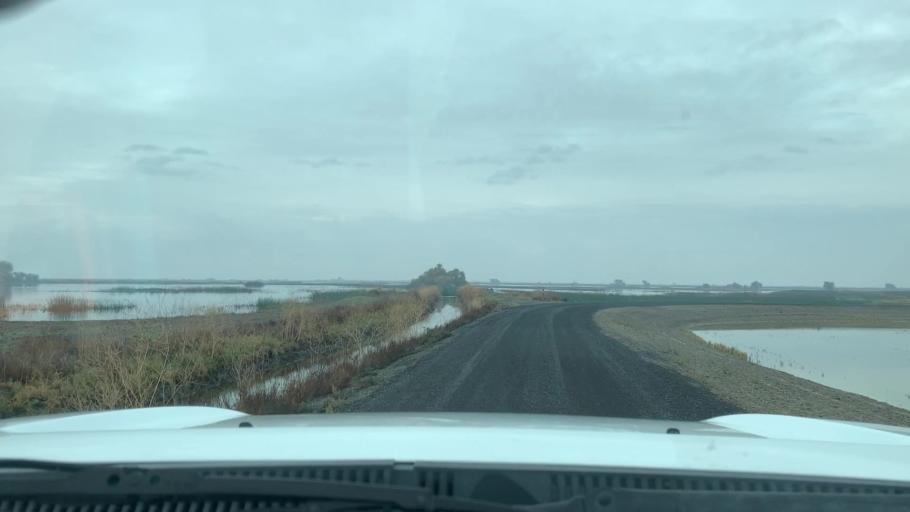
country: US
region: California
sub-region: Kern County
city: Lost Hills
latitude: 35.7371
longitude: -119.6104
